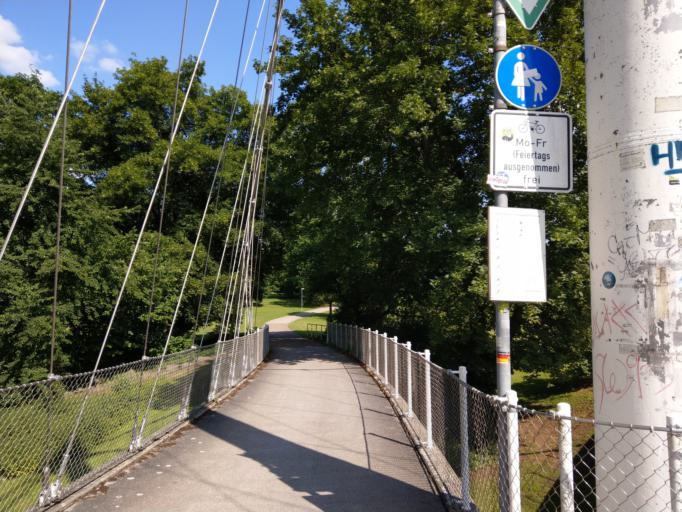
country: DE
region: Baden-Wuerttemberg
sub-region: Regierungsbezirk Stuttgart
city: Stuttgart Muehlhausen
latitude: 48.8339
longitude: 9.2095
